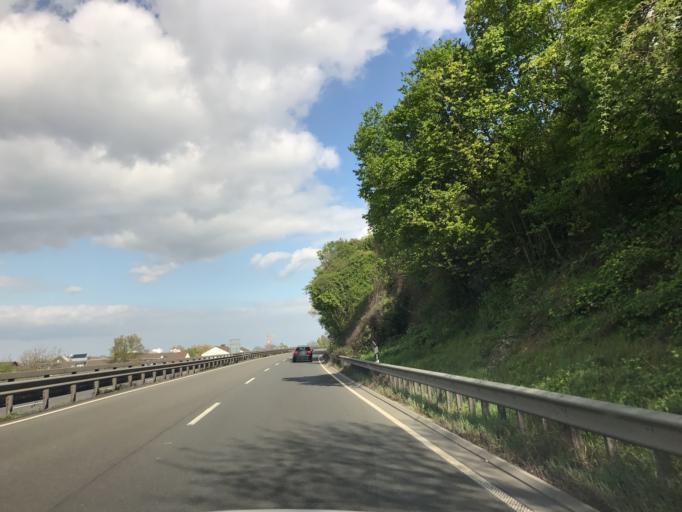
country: DE
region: North Rhine-Westphalia
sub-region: Regierungsbezirk Koln
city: Konigswinter
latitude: 50.6675
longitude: 7.1994
